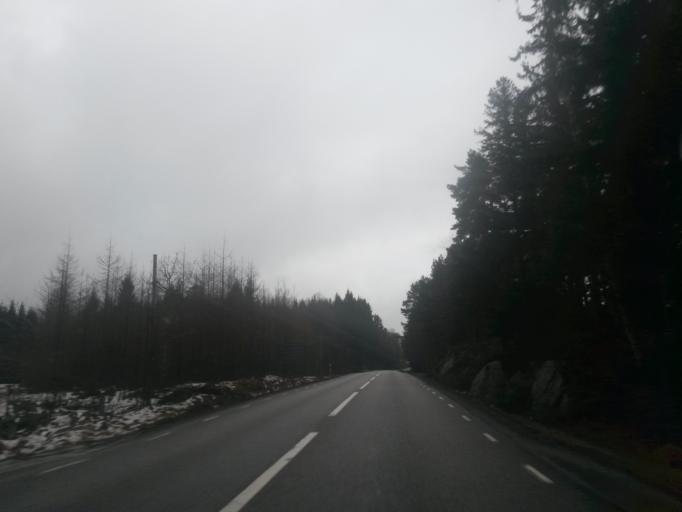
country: SE
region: Vaestra Goetaland
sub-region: Alingsas Kommun
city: Sollebrunn
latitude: 58.1302
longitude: 12.4934
